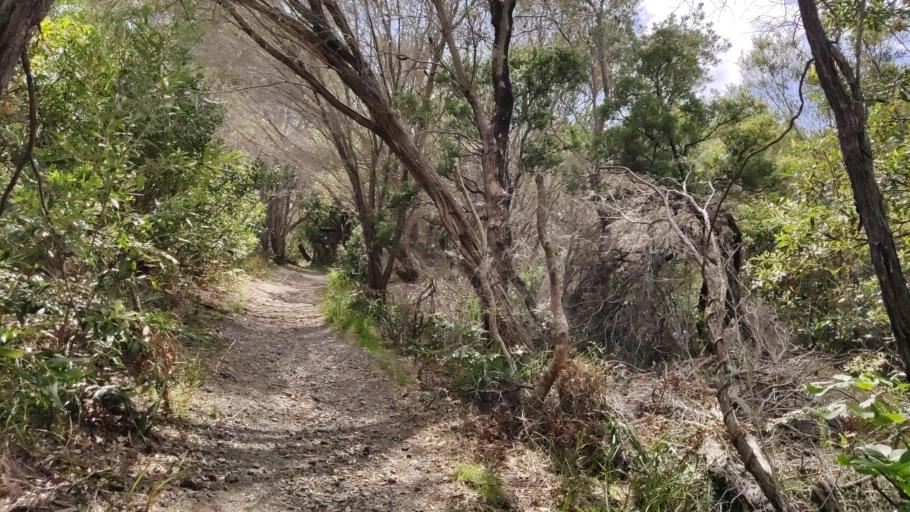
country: AU
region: New South Wales
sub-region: Port Macquarie-Hastings
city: North Haven
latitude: -31.6462
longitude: 152.8399
